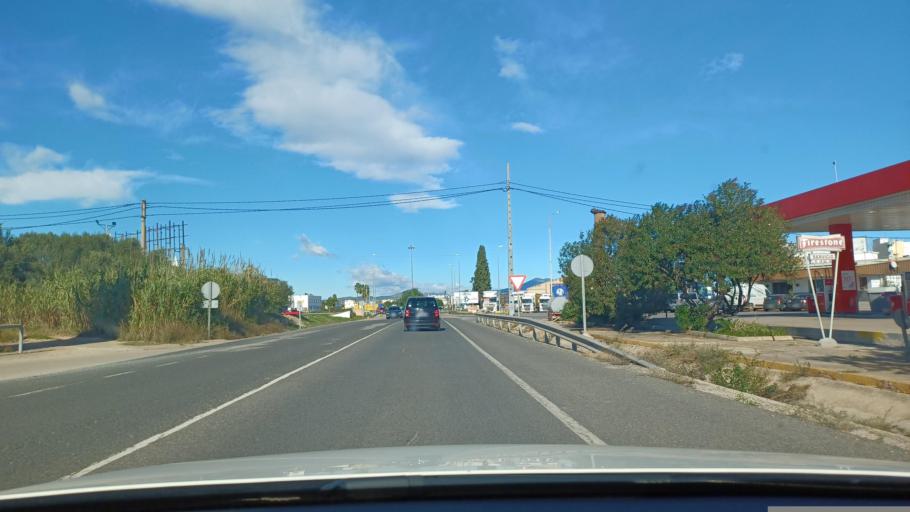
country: ES
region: Valencia
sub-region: Provincia de Castello
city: Vinaros
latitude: 40.4686
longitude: 0.4648
